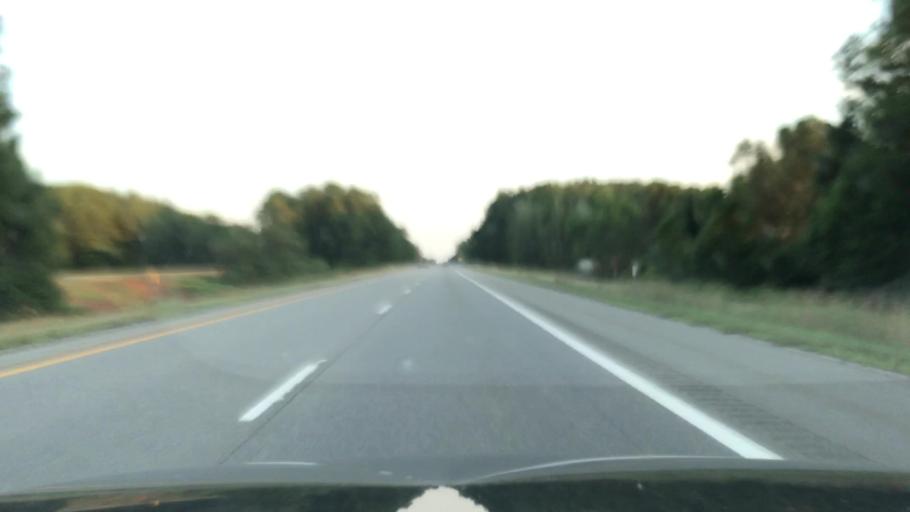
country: US
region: Michigan
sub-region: Montcalm County
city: Howard City
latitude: 43.5172
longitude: -85.4868
